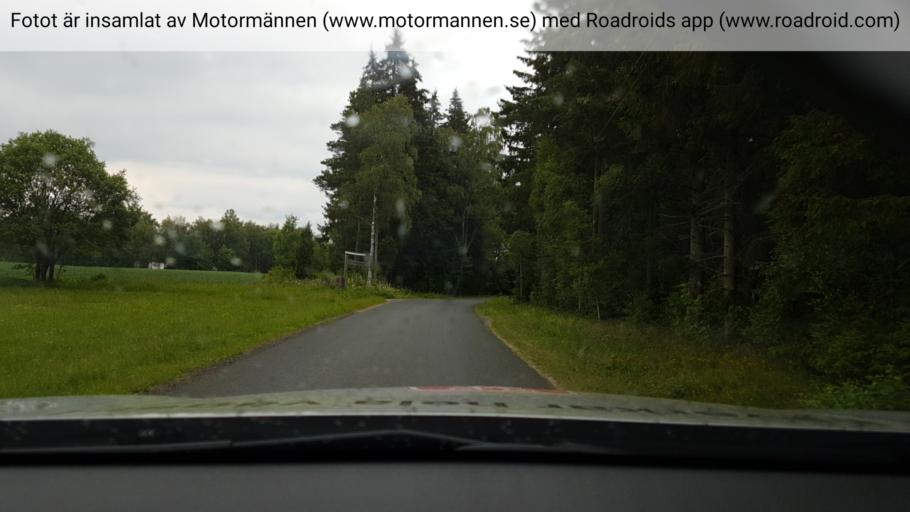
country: SE
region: Joenkoeping
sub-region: Mullsjo Kommun
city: Mullsjoe
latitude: 57.9739
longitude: 13.7517
